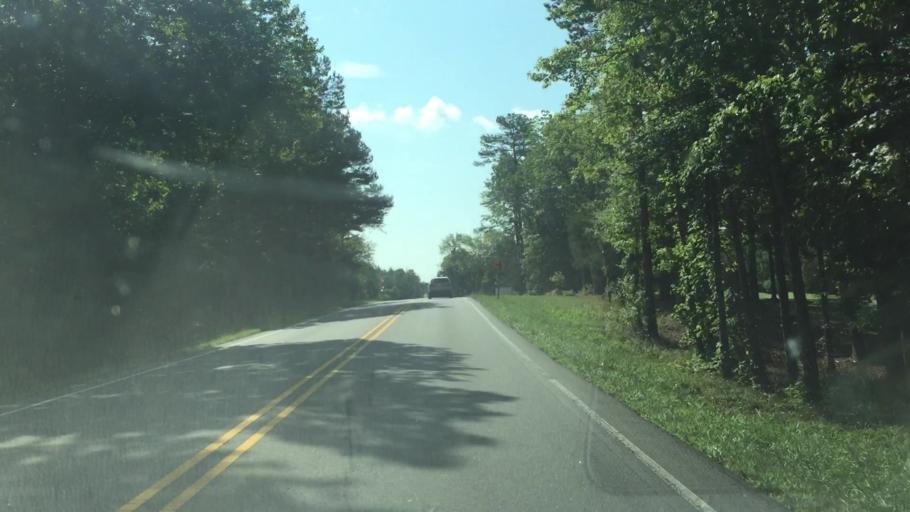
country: US
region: North Carolina
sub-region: Mecklenburg County
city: Mint Hill
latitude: 35.1712
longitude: -80.6055
